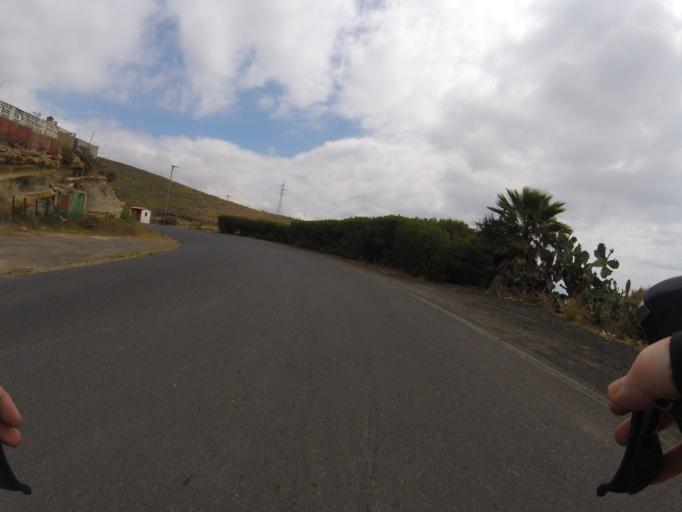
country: ES
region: Canary Islands
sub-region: Provincia de Santa Cruz de Tenerife
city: Guimar
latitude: 28.2871
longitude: -16.4047
